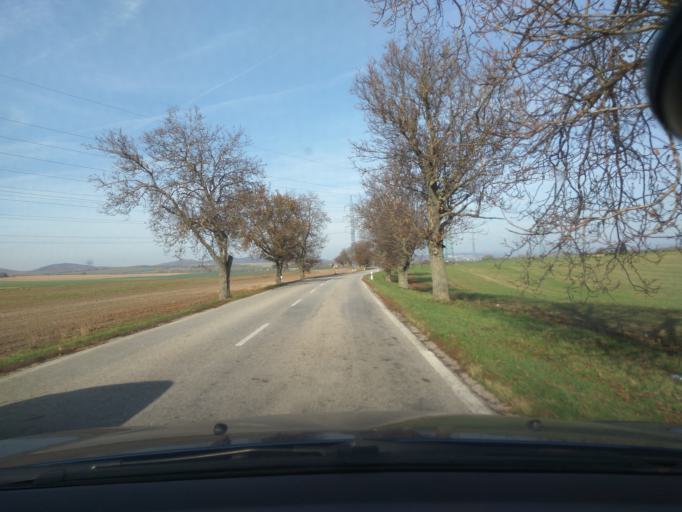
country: SK
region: Trnavsky
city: Vrbove
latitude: 48.6242
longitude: 17.7523
